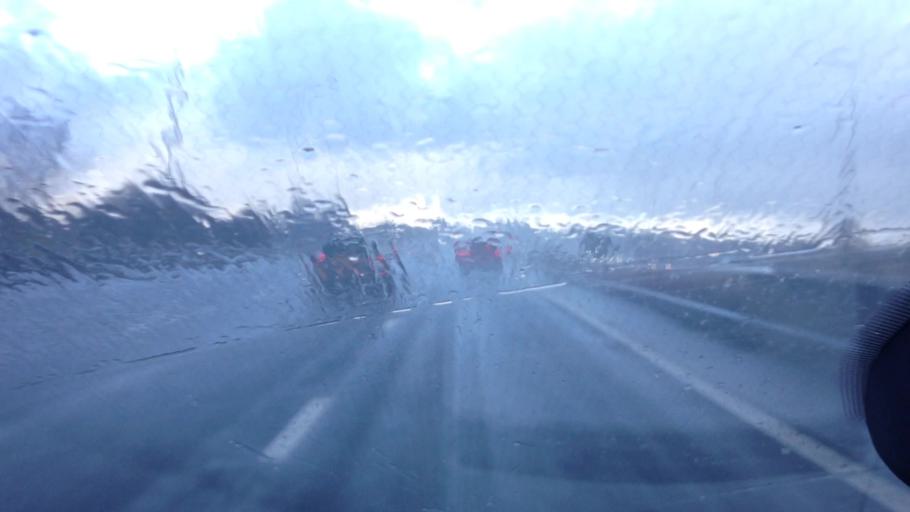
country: GB
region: England
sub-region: Kirklees
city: Cleckheaton
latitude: 53.7074
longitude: -1.7439
